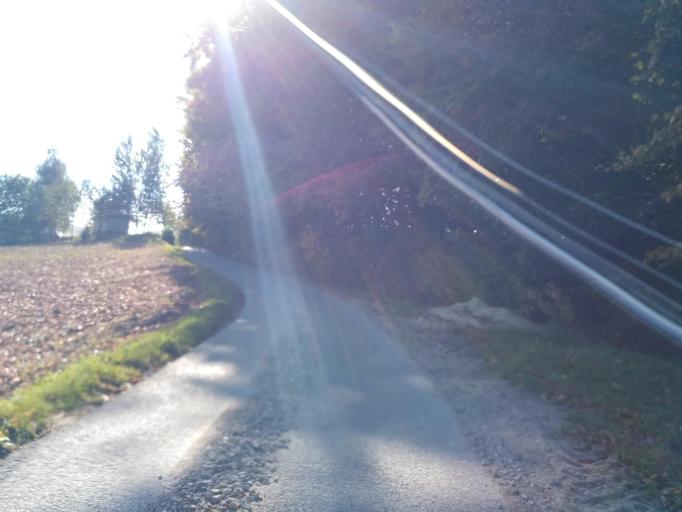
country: PL
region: Subcarpathian Voivodeship
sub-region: Powiat debicki
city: Slotowa
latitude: 49.9362
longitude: 21.2768
